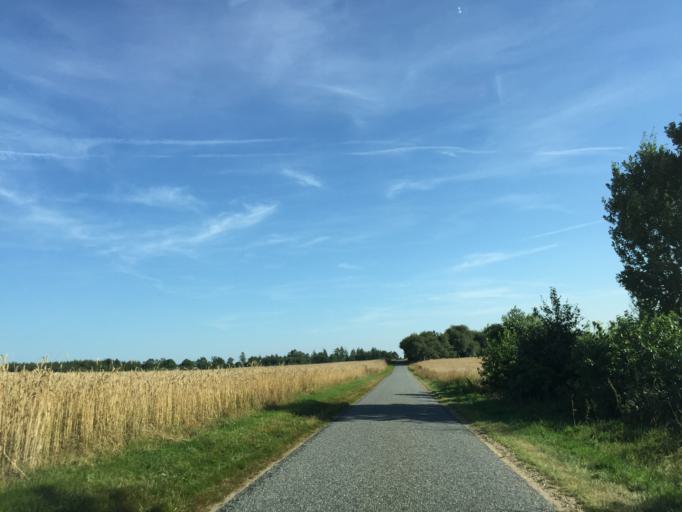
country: DK
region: Central Jutland
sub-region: Viborg Kommune
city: Bjerringbro
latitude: 56.2815
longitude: 9.6895
